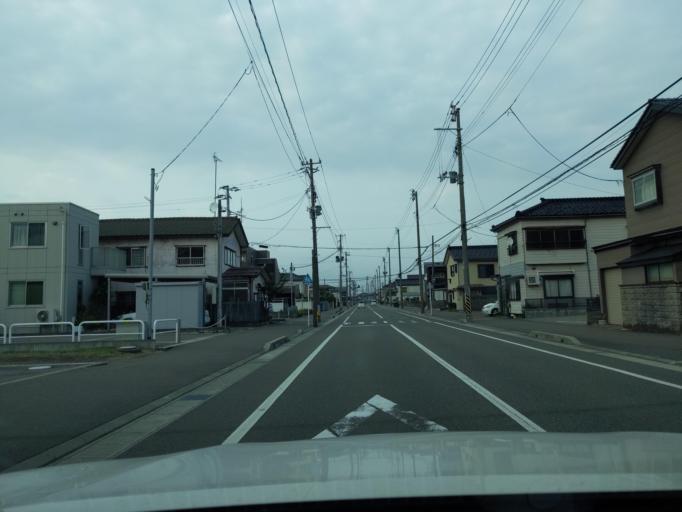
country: JP
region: Niigata
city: Kashiwazaki
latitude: 37.3776
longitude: 138.5632
